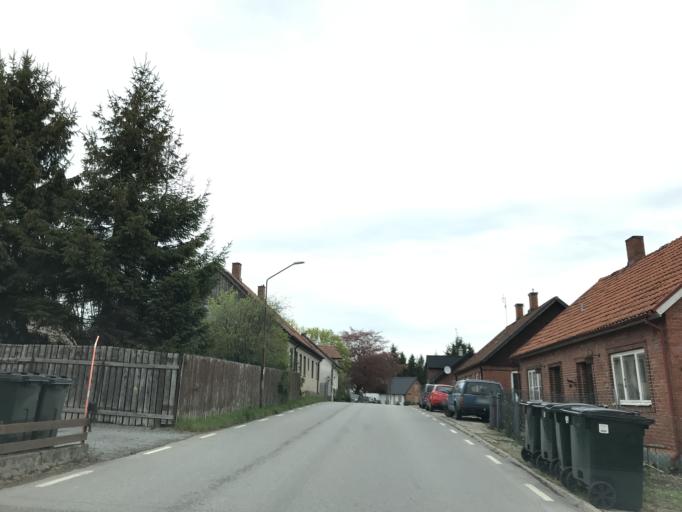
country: SE
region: Skane
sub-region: Trelleborgs Kommun
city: Anderslov
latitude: 55.4972
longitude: 13.3327
